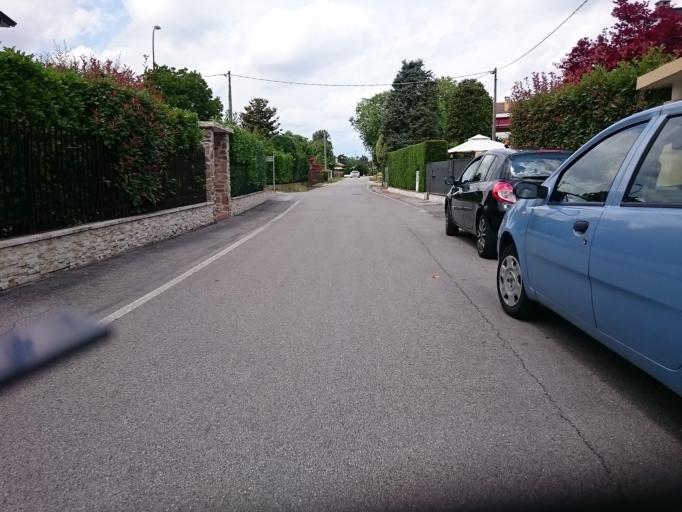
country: IT
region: Veneto
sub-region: Provincia di Padova
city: Caselle
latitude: 45.4156
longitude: 11.8234
